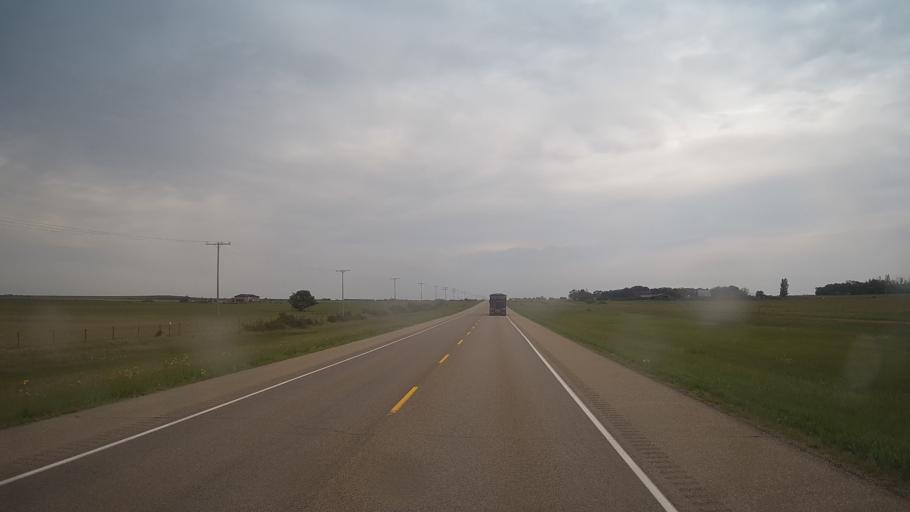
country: CA
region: Saskatchewan
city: Langham
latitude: 52.1290
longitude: -107.1602
